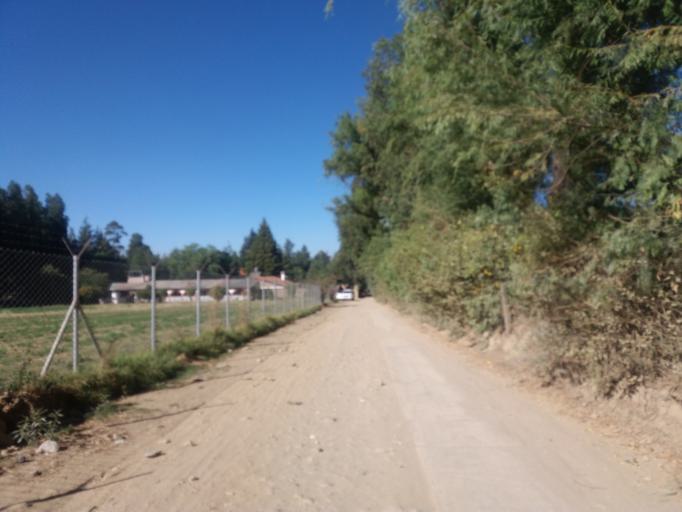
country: BO
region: Cochabamba
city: Cochabamba
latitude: -17.3451
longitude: -66.2169
